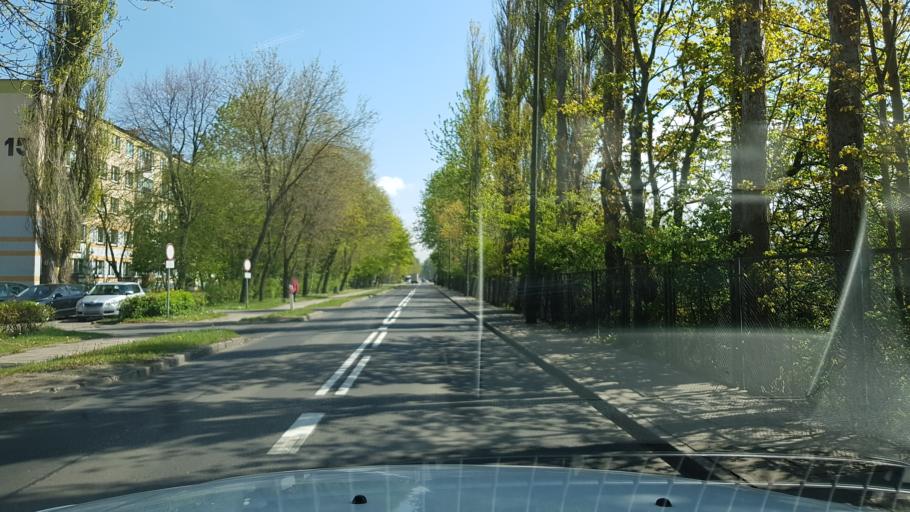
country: PL
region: Pomeranian Voivodeship
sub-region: Powiat slupski
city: Ustka
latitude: 54.5778
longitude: 16.8641
